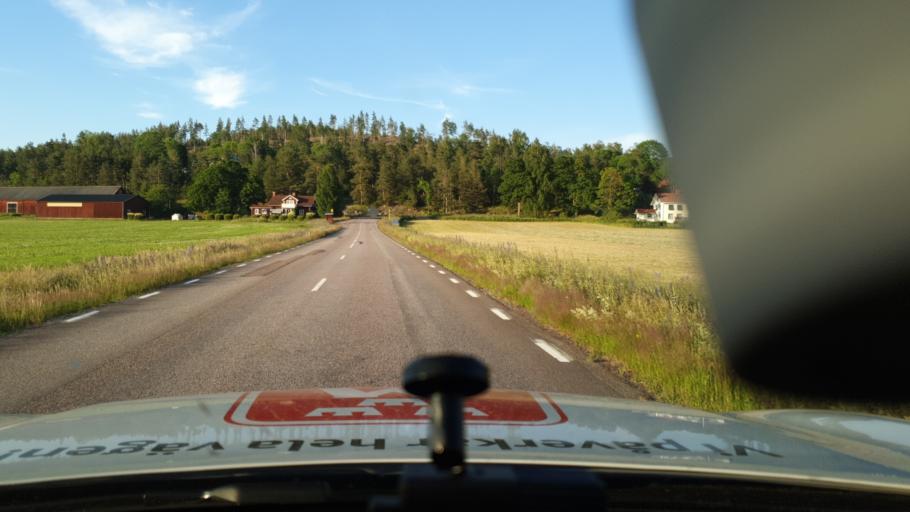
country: SE
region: Vaermland
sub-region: Kils Kommun
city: Kil
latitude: 59.6152
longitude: 13.3230
